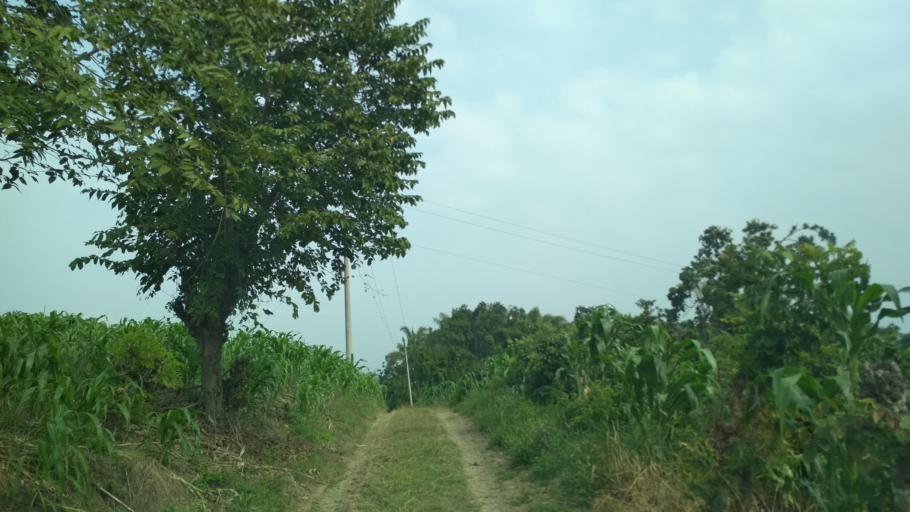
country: MM
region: Kayah
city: Loikaw
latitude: 20.2049
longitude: 97.3233
